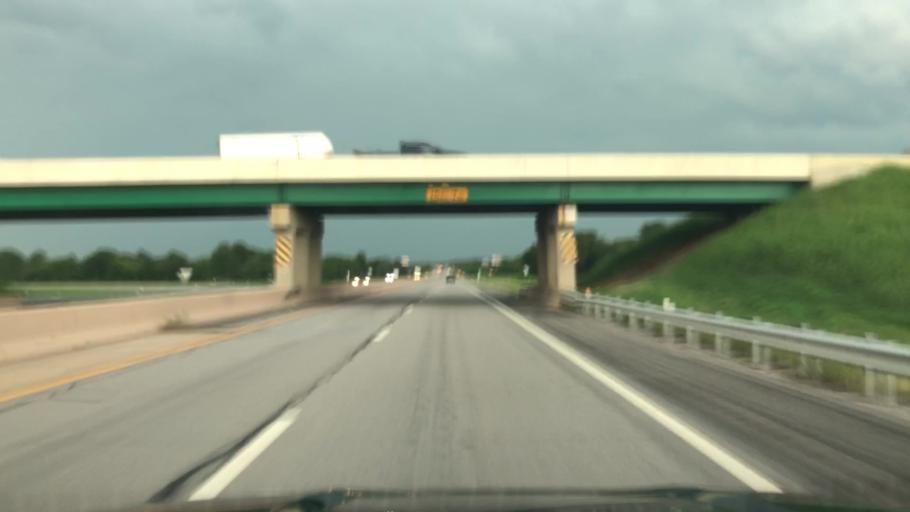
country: US
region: Oklahoma
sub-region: Rogers County
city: Justice
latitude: 36.3013
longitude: -95.5910
